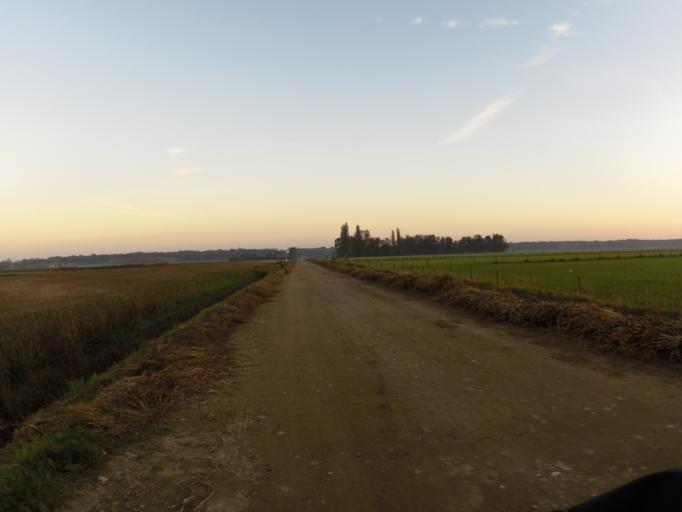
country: NL
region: North Brabant
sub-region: Gemeente Vught
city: Vught
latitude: 51.6787
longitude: 5.2726
